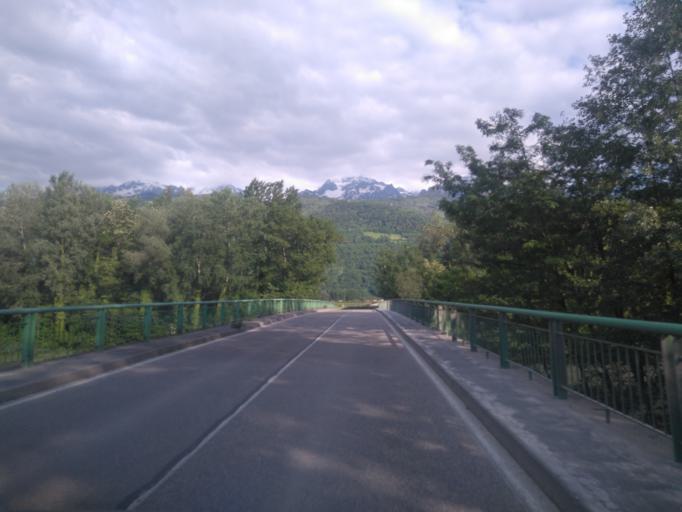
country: FR
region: Rhone-Alpes
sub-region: Departement de l'Isere
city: Le Versoud
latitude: 45.2307
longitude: 5.8538
